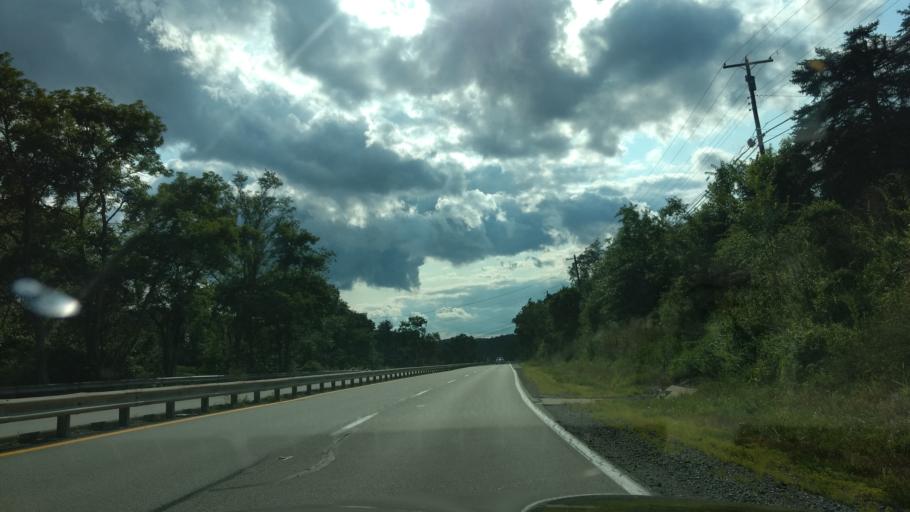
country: US
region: Pennsylvania
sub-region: Westmoreland County
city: Murrysville
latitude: 40.5113
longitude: -79.6493
